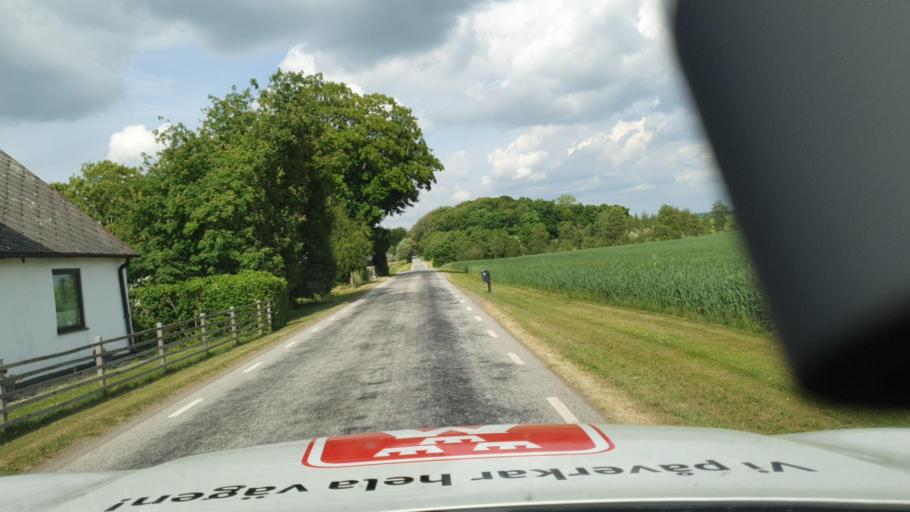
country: SE
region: Skane
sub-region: Skurups Kommun
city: Skurup
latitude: 55.5078
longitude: 13.4929
